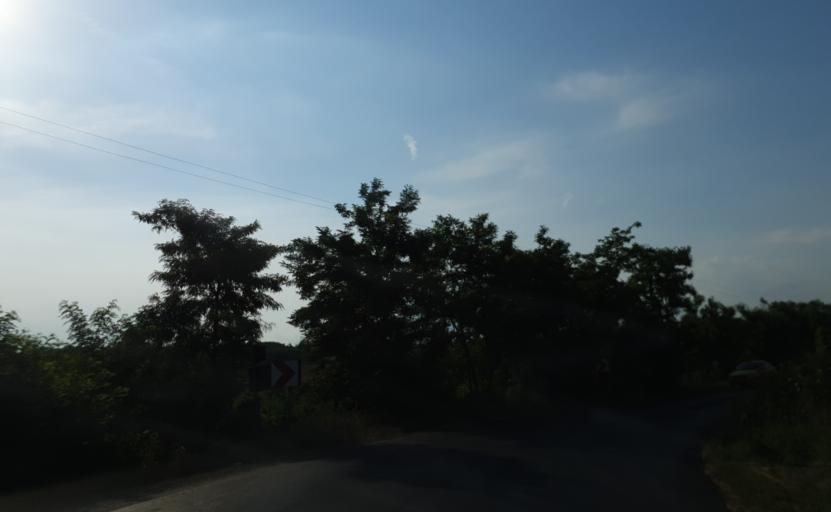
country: TR
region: Tekirdag
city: Muratli
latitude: 41.1964
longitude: 27.4702
